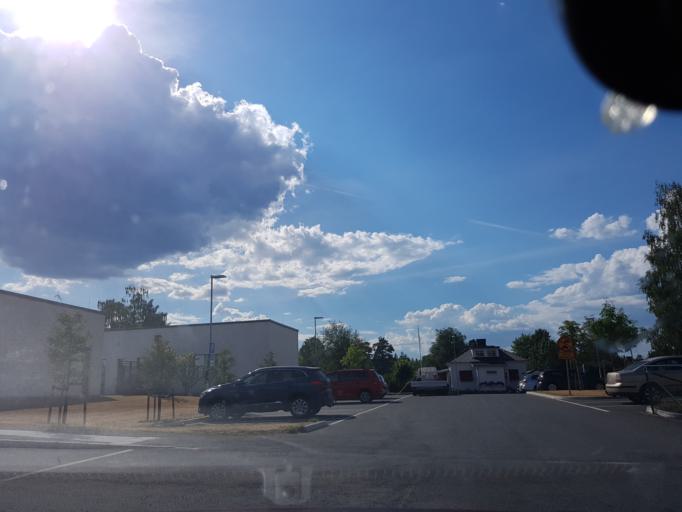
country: SE
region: Joenkoeping
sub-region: Gislaveds Kommun
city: Gislaved
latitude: 57.3054
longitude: 13.5379
